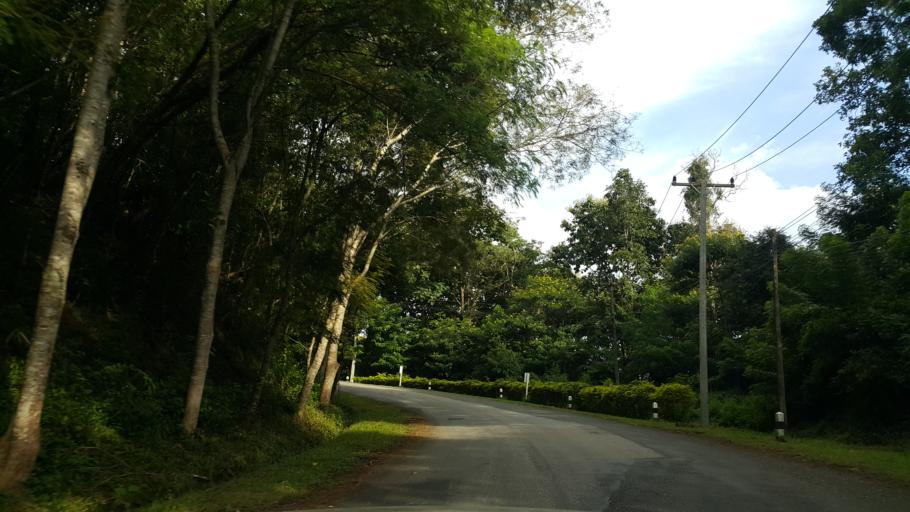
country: TH
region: Chiang Mai
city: Mae On
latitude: 18.8857
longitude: 99.2209
